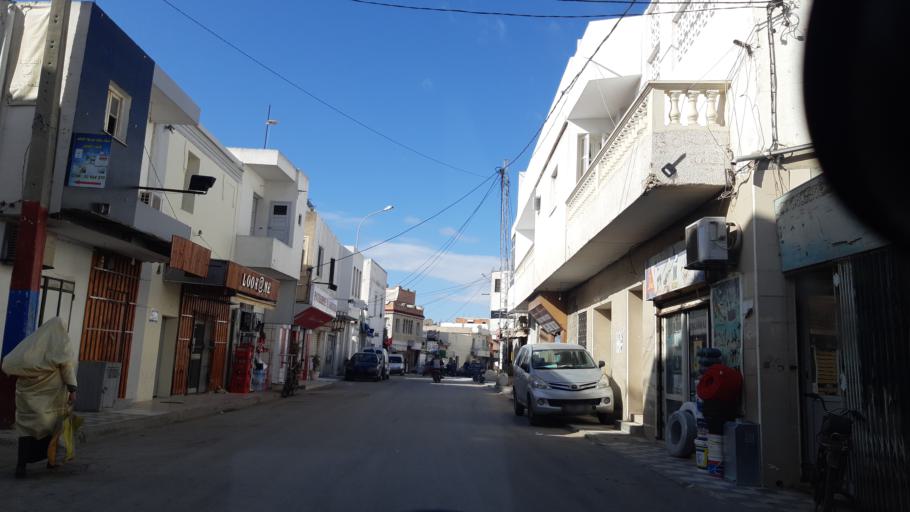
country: TN
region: Susah
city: Akouda
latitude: 35.8701
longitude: 10.5363
